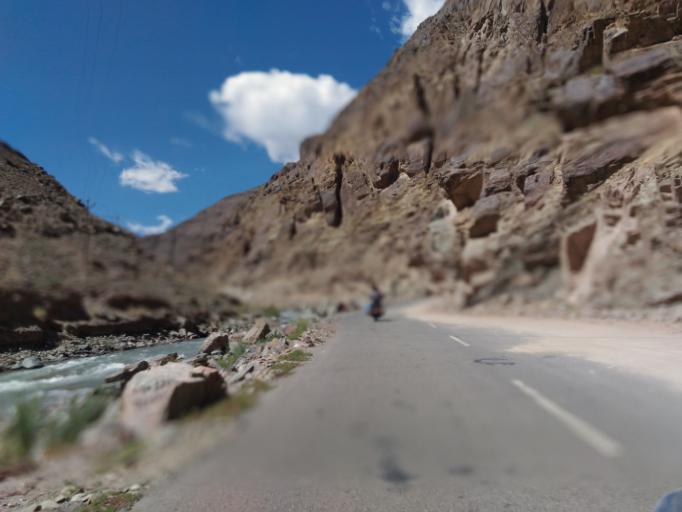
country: IN
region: Kashmir
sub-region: Ladakh
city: Leh
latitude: 33.8055
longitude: 77.7982
